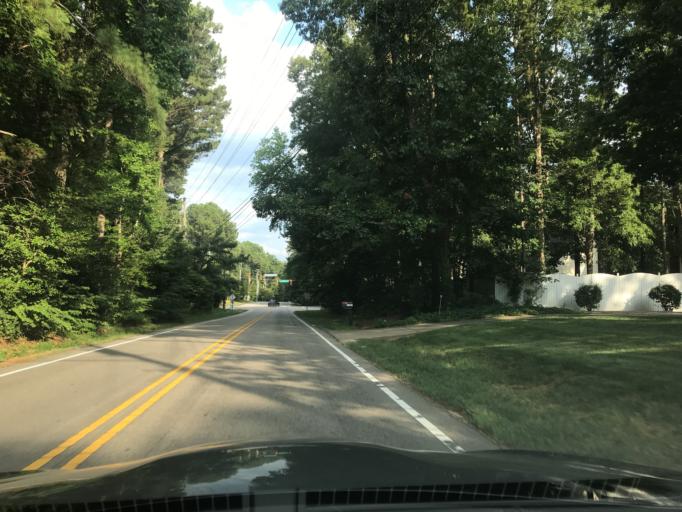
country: US
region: North Carolina
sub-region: Wake County
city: West Raleigh
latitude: 35.8791
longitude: -78.7066
